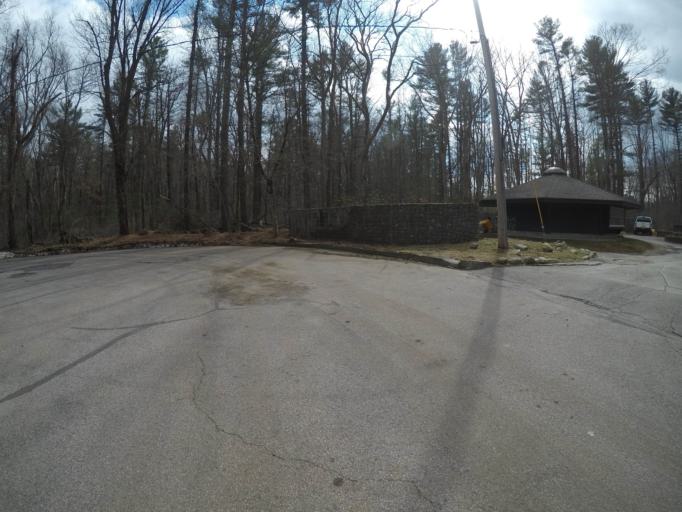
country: US
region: Massachusetts
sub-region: Bristol County
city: Easton
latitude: 42.0444
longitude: -71.1219
